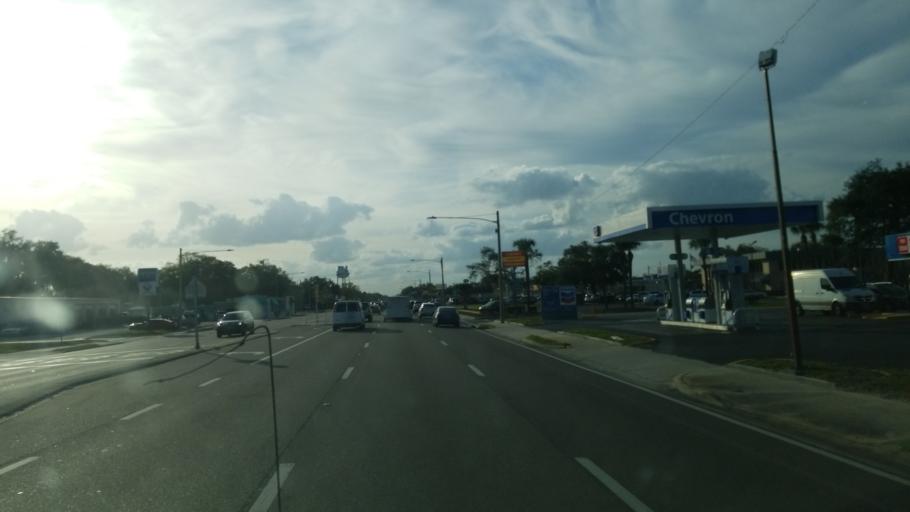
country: US
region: Florida
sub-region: Osceola County
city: Saint Cloud
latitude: 28.2460
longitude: -81.2772
